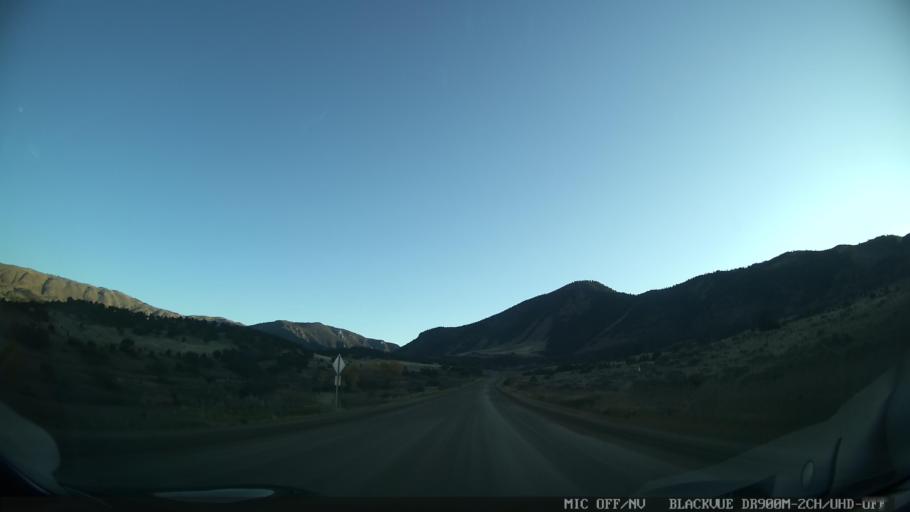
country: US
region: Colorado
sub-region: Grand County
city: Kremmling
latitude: 39.9741
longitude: -106.5037
